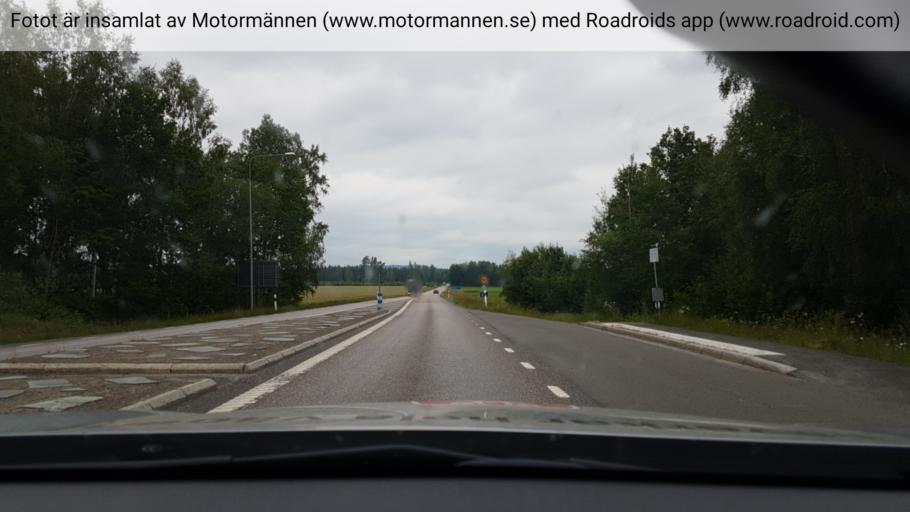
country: SE
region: Vaestra Goetaland
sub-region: Skovde Kommun
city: Skultorp
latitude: 58.2543
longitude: 13.8135
